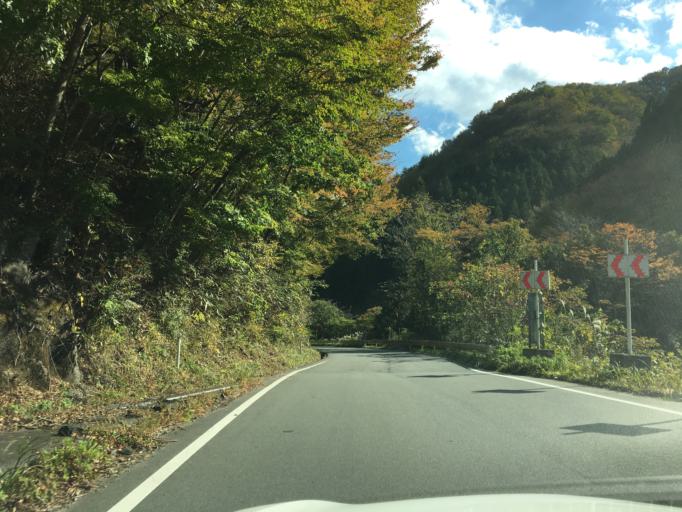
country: JP
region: Fukushima
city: Namie
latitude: 37.3502
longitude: 140.8989
